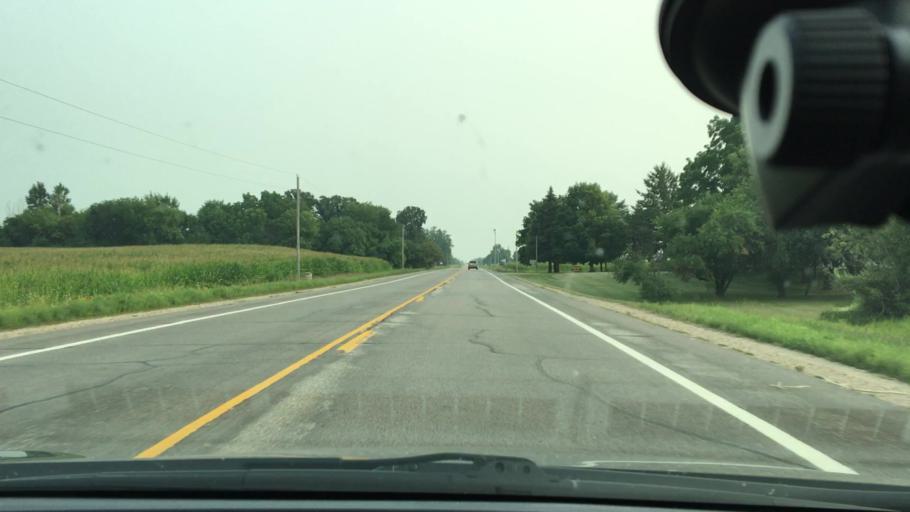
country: US
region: Minnesota
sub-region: Wright County
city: Albertville
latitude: 45.2791
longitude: -93.6637
